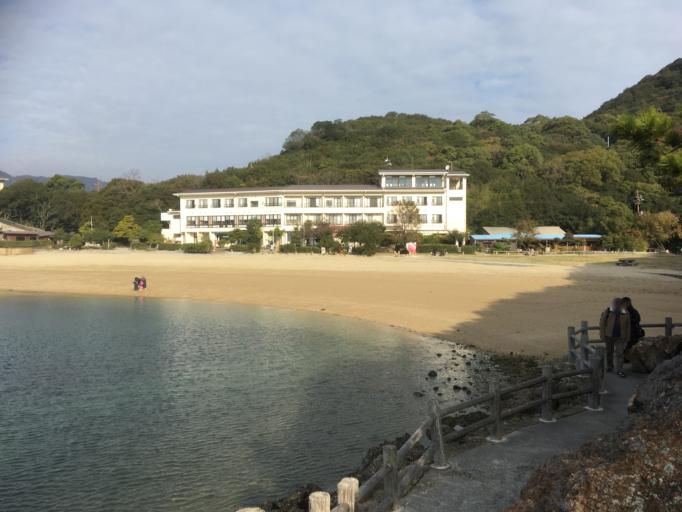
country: JP
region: Hiroshima
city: Fukuyama
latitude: 34.3828
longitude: 133.3916
